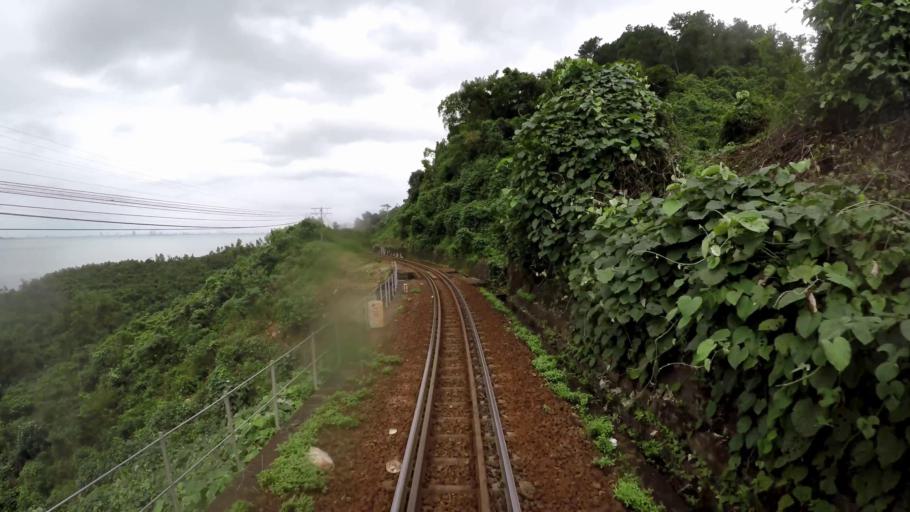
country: VN
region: Da Nang
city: Lien Chieu
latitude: 16.1606
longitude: 108.1344
